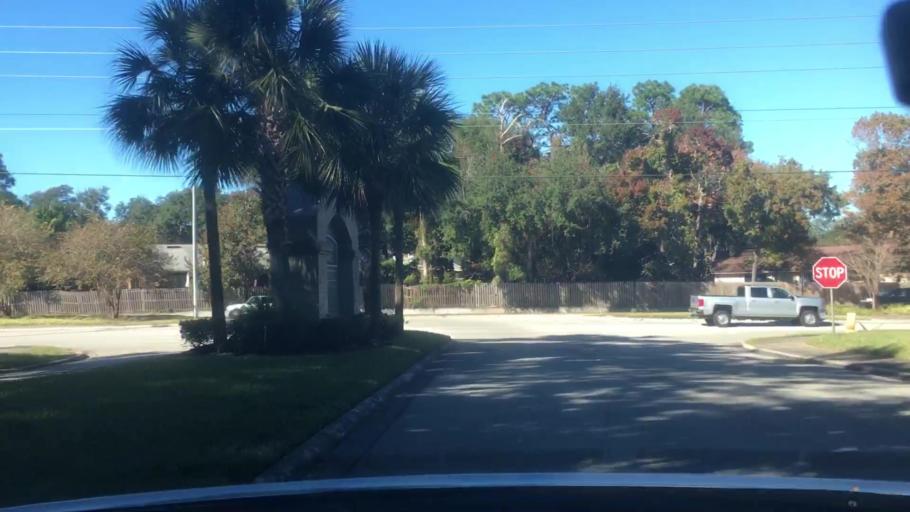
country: US
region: Florida
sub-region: Duval County
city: Jacksonville
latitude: 30.3435
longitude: -81.5340
